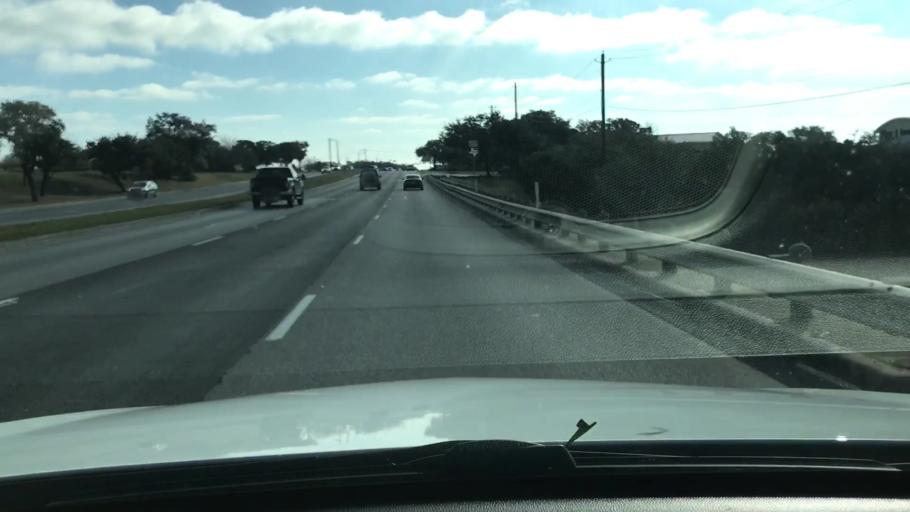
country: US
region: Texas
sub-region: Travis County
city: Bee Cave
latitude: 30.3065
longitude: -97.9403
